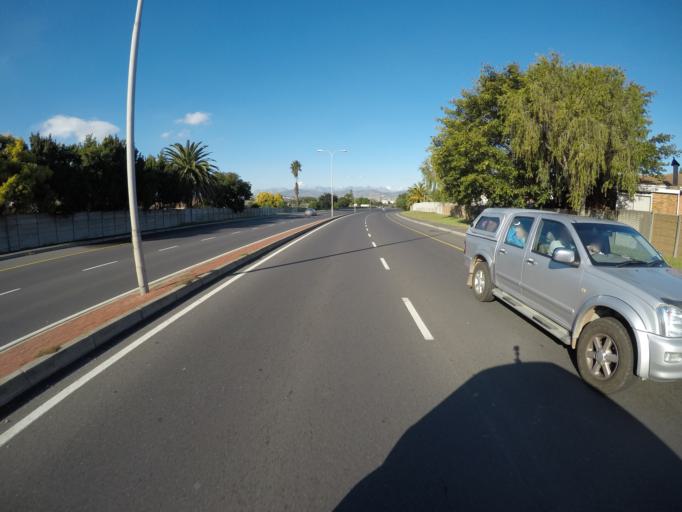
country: ZA
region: Western Cape
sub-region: City of Cape Town
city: Kraaifontein
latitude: -33.8840
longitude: 18.6678
